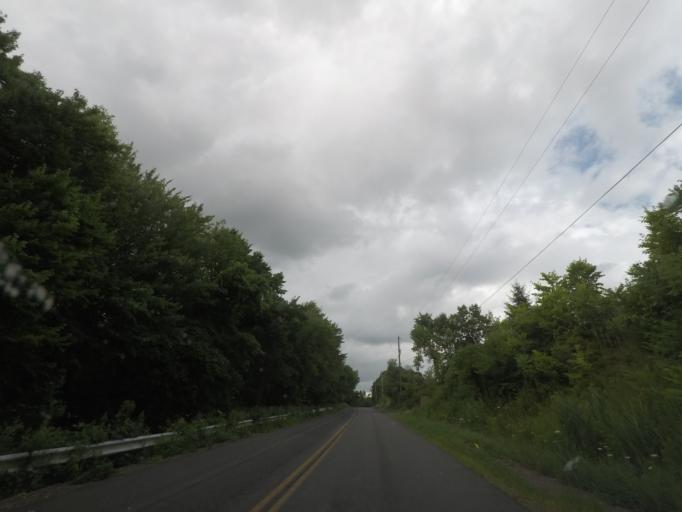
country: US
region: New York
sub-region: Rensselaer County
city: West Sand Lake
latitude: 42.6484
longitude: -73.6291
